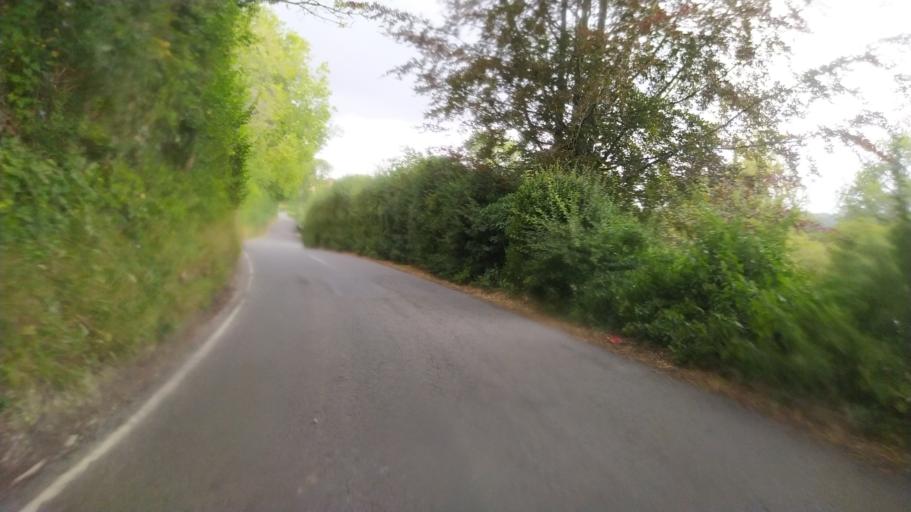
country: GB
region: England
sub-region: Hampshire
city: Four Marks
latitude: 51.0026
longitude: -1.0449
